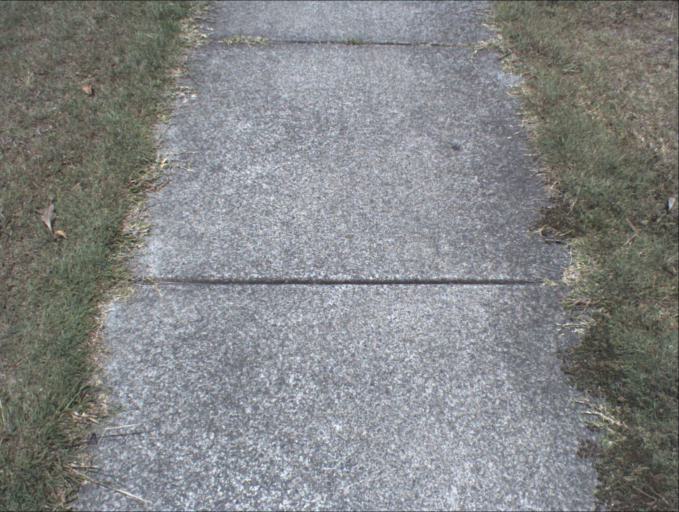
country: AU
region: Queensland
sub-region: Logan
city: Windaroo
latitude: -27.7305
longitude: 153.2094
